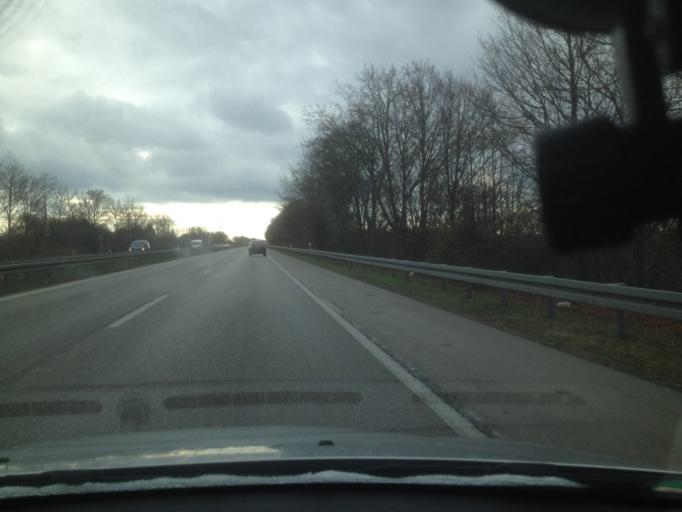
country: DE
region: Bavaria
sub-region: Swabia
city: Konigsbrunn
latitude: 48.3154
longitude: 10.8858
